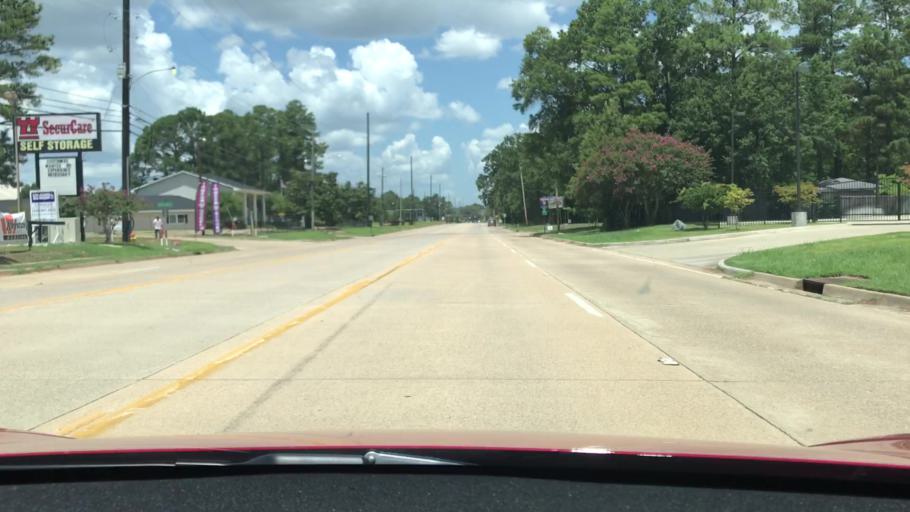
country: US
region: Louisiana
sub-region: Bossier Parish
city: Bossier City
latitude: 32.4245
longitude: -93.7391
